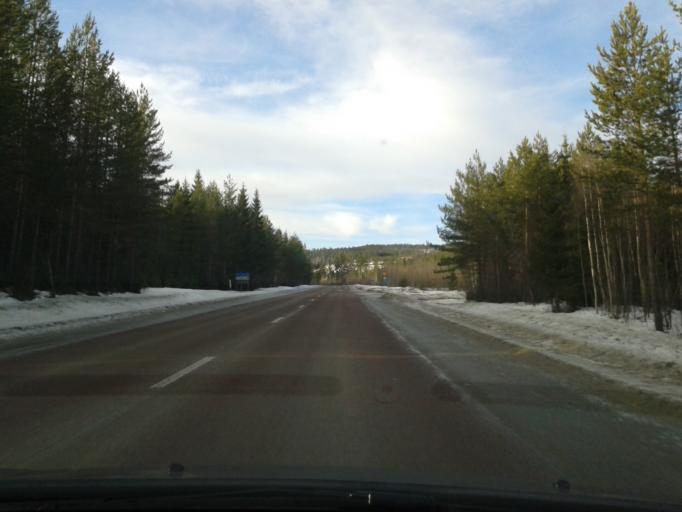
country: SE
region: Vaesternorrland
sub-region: OErnskoeldsviks Kommun
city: Bjasta
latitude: 63.3771
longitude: 18.4248
